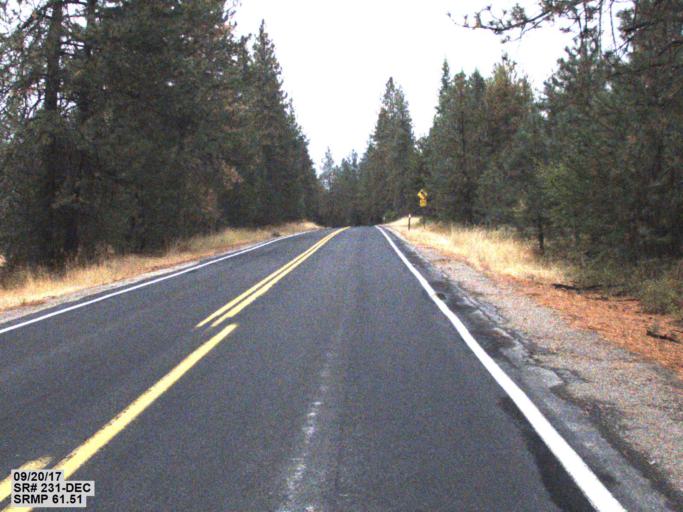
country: US
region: Washington
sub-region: Stevens County
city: Chewelah
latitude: 48.0476
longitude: -117.7415
